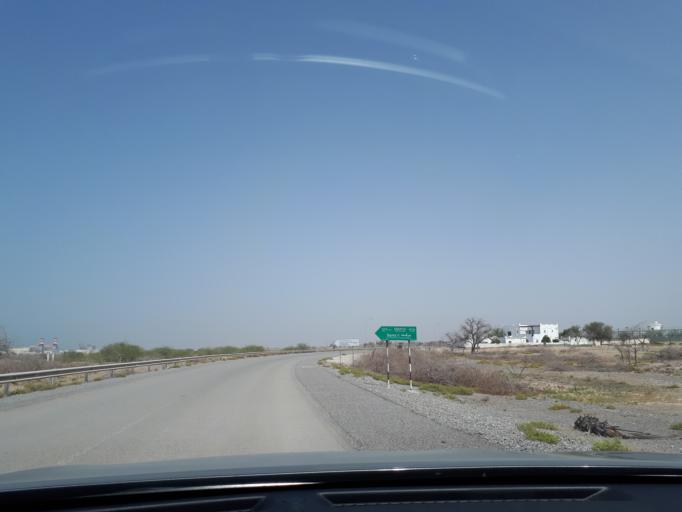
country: OM
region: Al Batinah
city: Barka'
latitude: 23.7022
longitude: 57.9579
